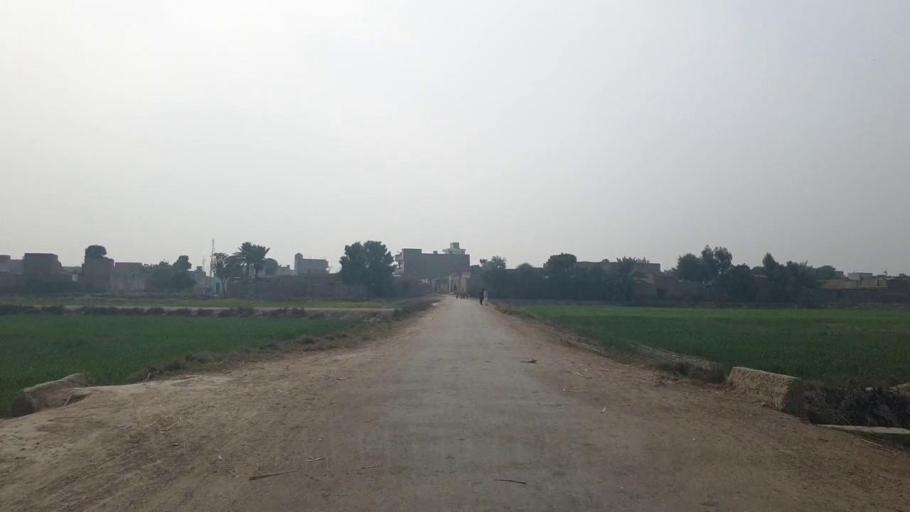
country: PK
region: Sindh
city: Tando Adam
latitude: 25.7797
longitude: 68.6688
